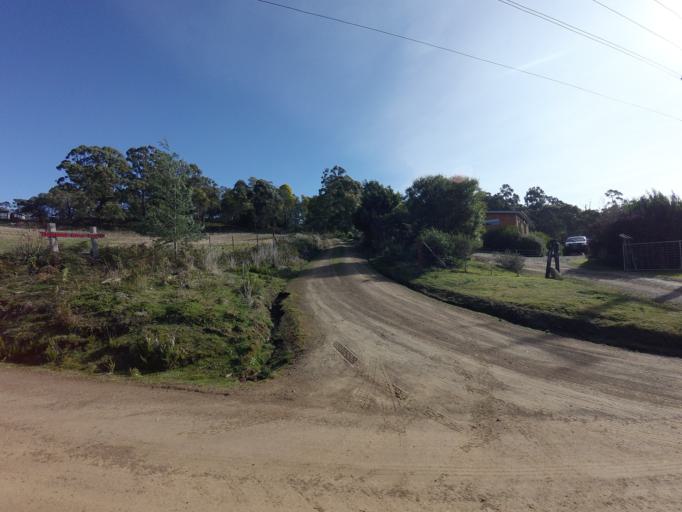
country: AU
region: Tasmania
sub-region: Kingborough
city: Kettering
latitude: -43.0865
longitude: 147.2644
